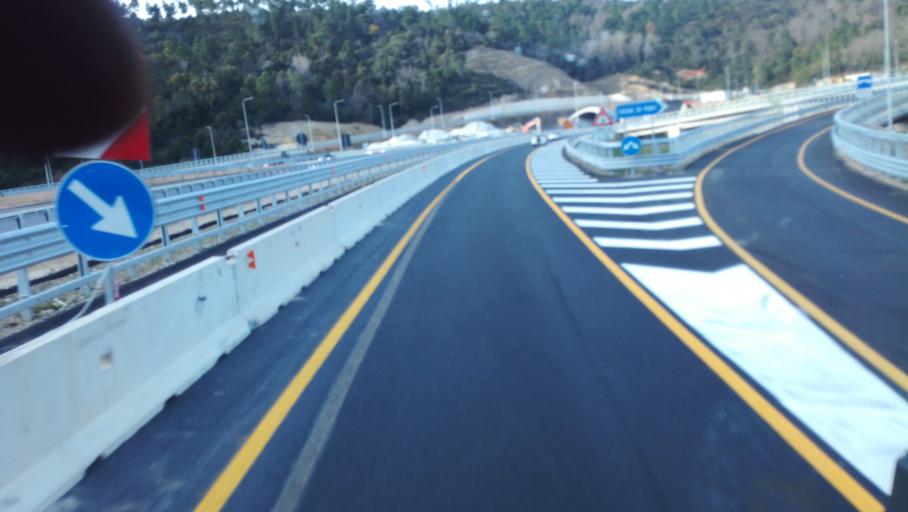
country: IT
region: Tuscany
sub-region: Provincia di Grosseto
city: Civitella Marittima
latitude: 43.0508
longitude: 11.2841
